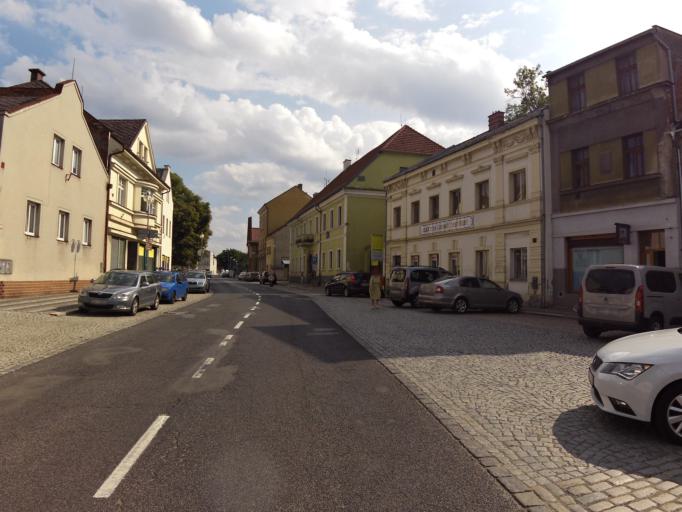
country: CZ
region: Central Bohemia
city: Mnichovo Hradiste
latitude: 50.5242
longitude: 14.9732
